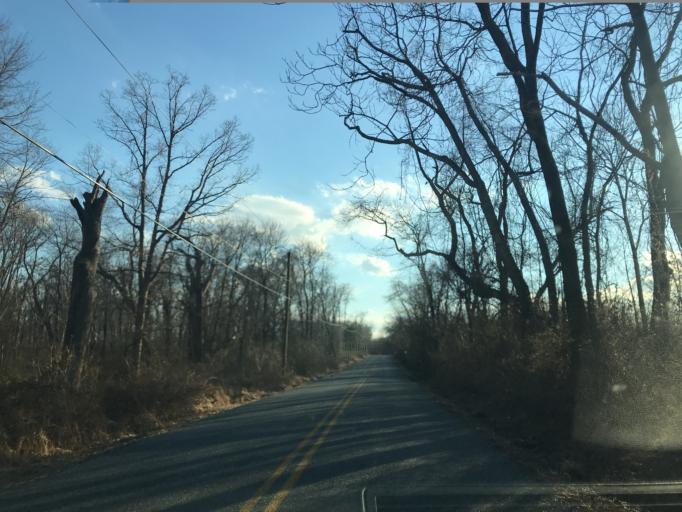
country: US
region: Pennsylvania
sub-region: York County
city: Susquehanna Trails
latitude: 39.6775
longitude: -76.2479
